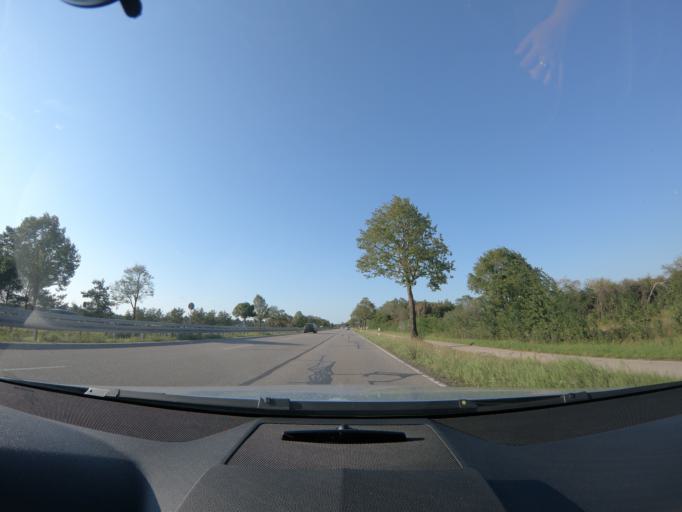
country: DE
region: Bavaria
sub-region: Upper Bavaria
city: Oberschleissheim
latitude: 48.2163
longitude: 11.5879
